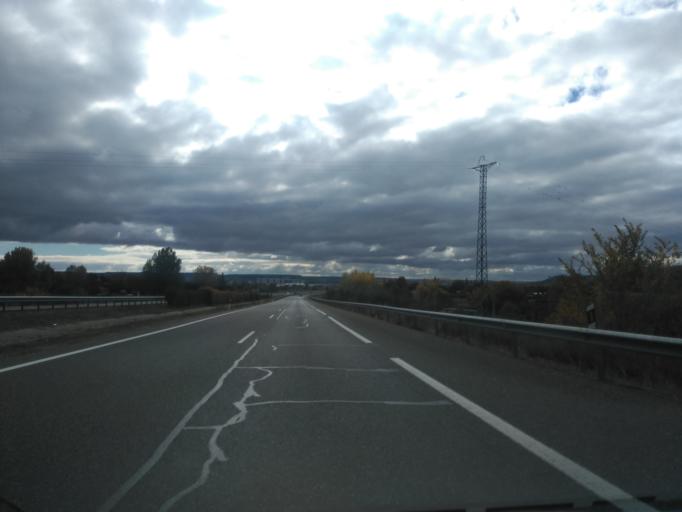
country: ES
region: Castille and Leon
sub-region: Provincia de Palencia
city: Villamuriel de Cerrato
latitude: 41.9783
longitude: -4.5011
